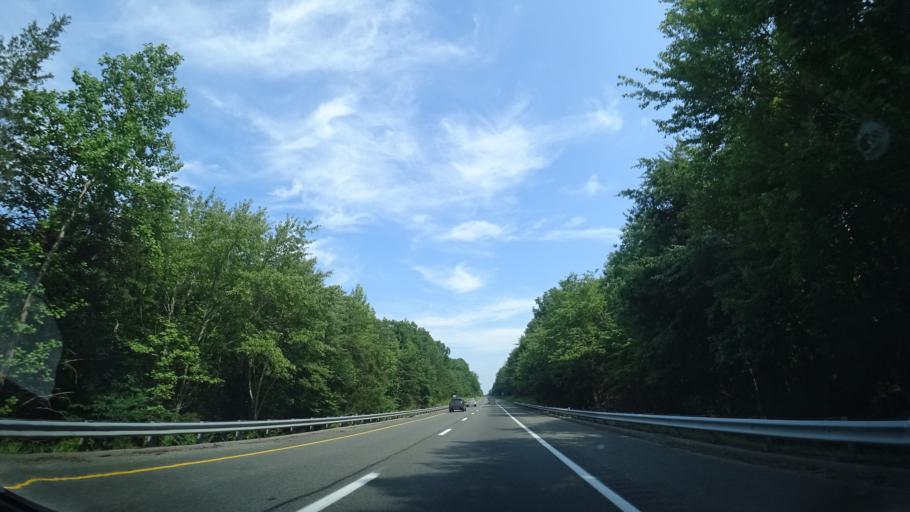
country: US
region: Virginia
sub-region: Goochland County
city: Goochland
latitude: 37.8379
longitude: -77.9753
